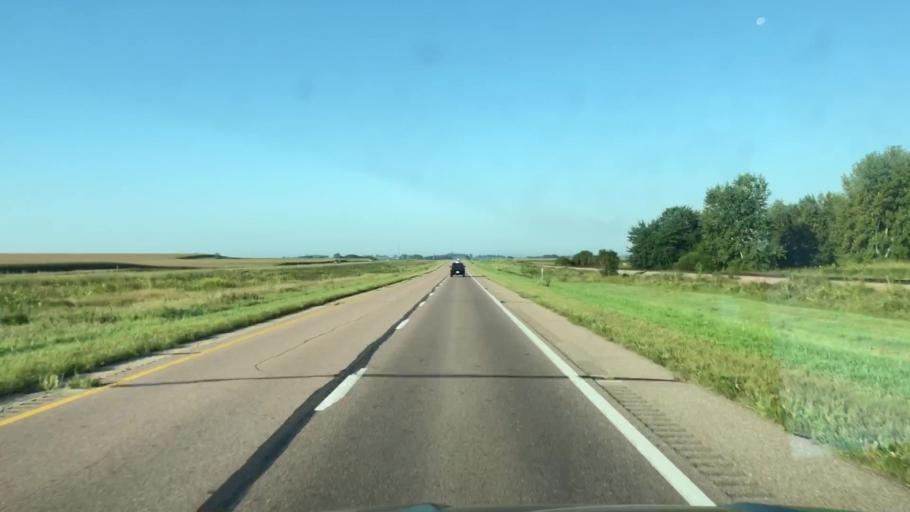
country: US
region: Iowa
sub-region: Sioux County
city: Alton
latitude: 43.0242
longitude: -95.9457
